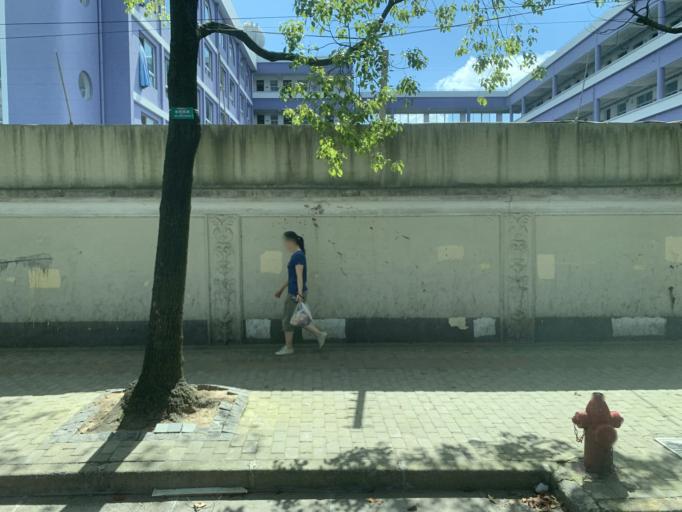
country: CN
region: Shanghai Shi
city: Huamu
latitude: 31.1735
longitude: 121.5361
